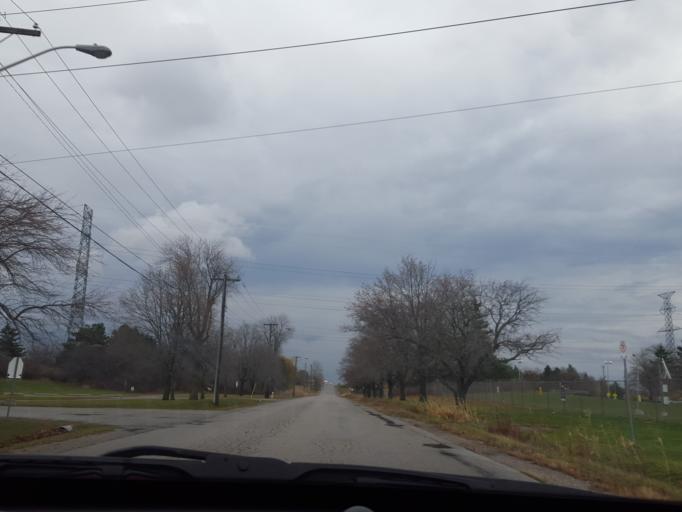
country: CA
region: Ontario
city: Ajax
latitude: 43.8139
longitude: -79.0671
